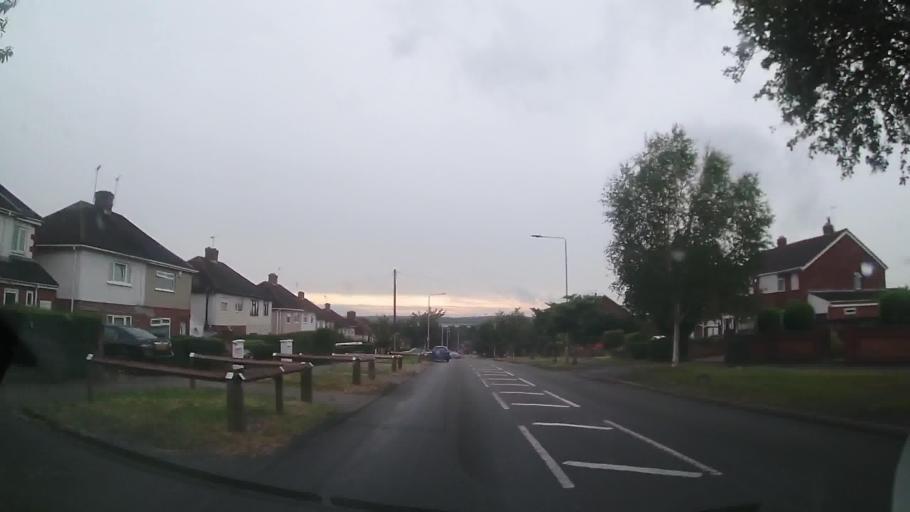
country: GB
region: England
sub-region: Leicestershire
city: Glenfield
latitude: 52.6444
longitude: -1.1985
